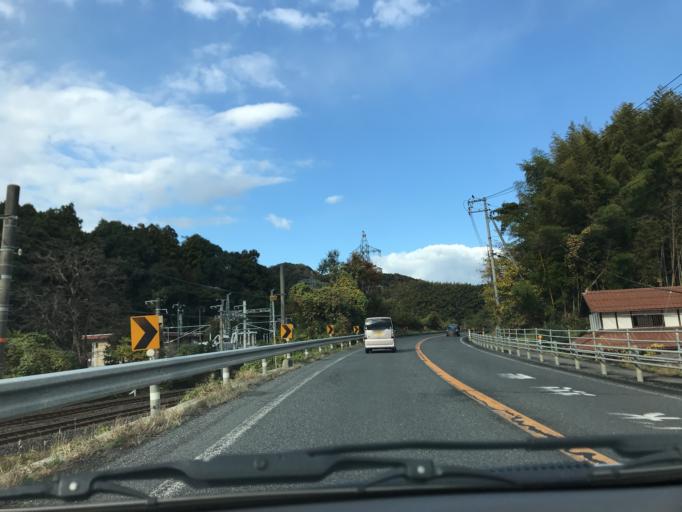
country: JP
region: Tottori
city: Yonago
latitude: 35.4084
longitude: 133.2984
